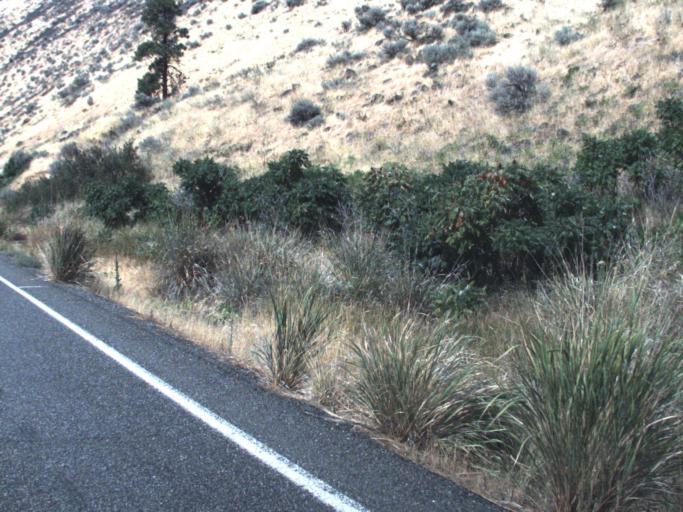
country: US
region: Washington
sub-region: Kittitas County
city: Kittitas
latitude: 46.8687
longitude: -120.4807
